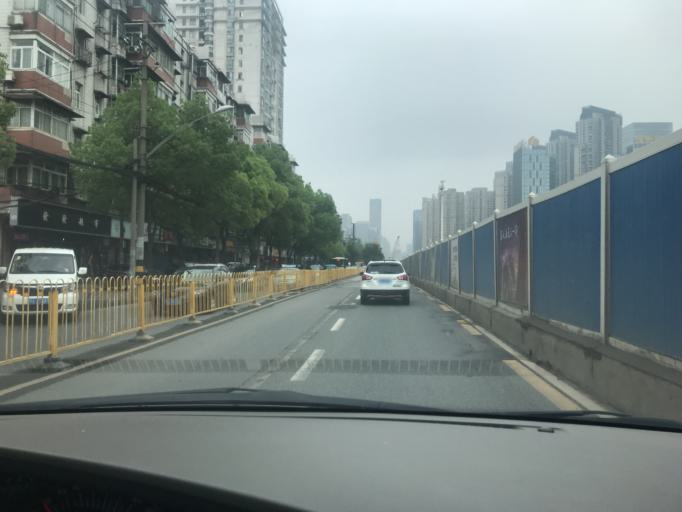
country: CN
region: Hubei
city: Jiang'an
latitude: 30.5880
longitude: 114.3237
